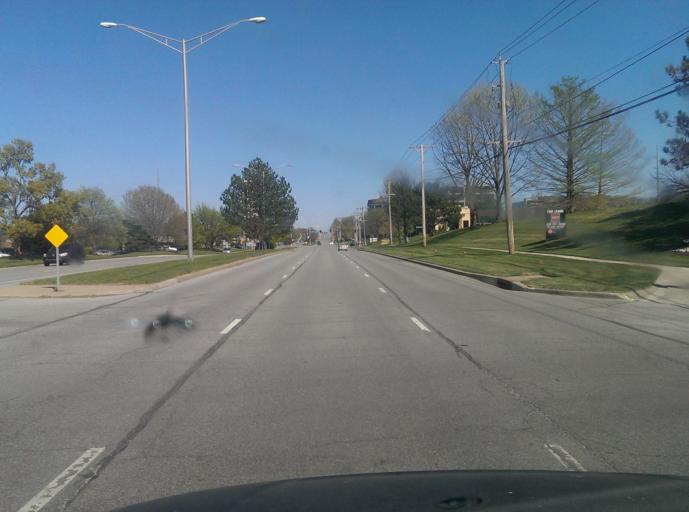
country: US
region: Kansas
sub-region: Johnson County
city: Overland Park
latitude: 38.9274
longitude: -94.6658
